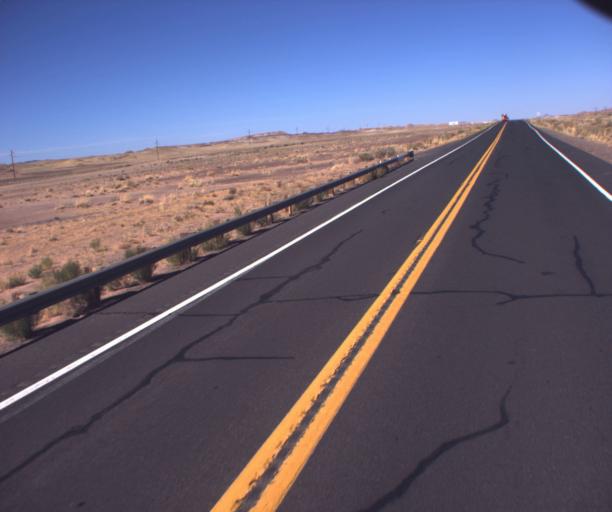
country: US
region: Arizona
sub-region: Coconino County
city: Tuba City
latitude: 35.9415
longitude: -111.3998
